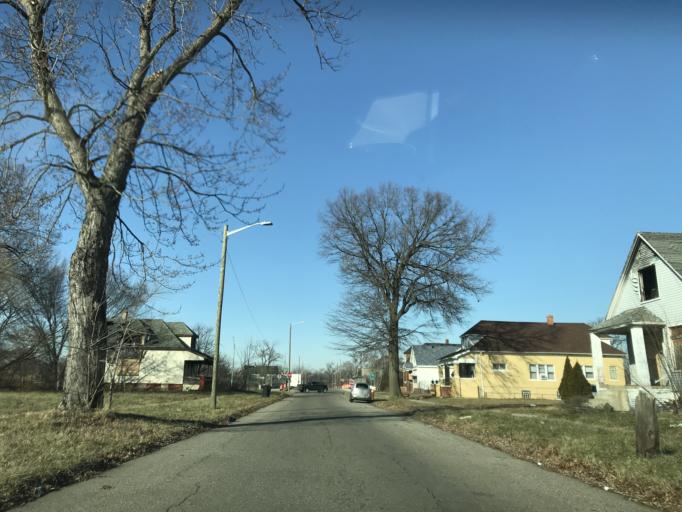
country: US
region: Michigan
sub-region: Wayne County
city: Dearborn
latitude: 42.3419
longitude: -83.1143
